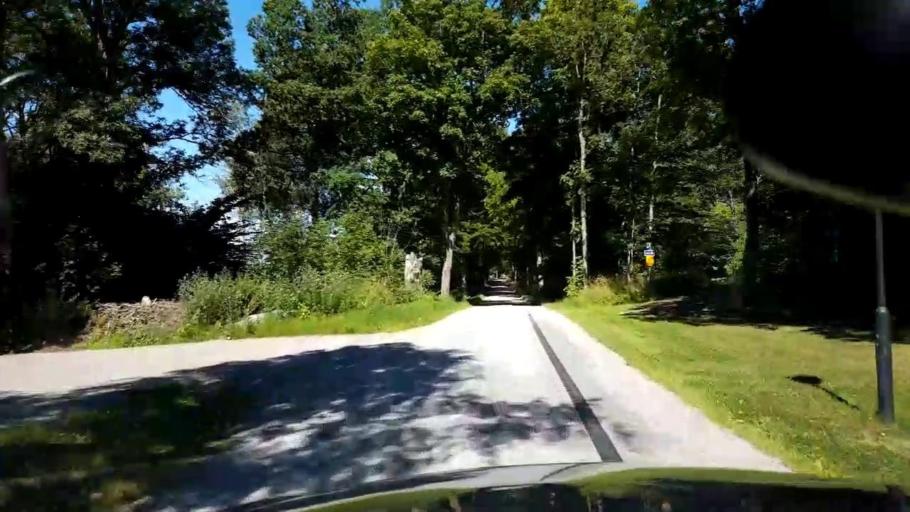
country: SE
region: Stockholm
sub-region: Sigtuna Kommun
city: Sigtuna
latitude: 59.6091
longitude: 17.6401
